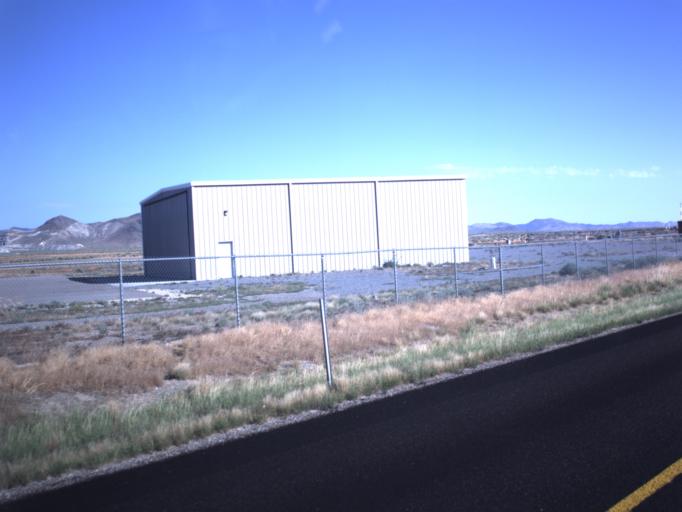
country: US
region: Utah
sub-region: Beaver County
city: Milford
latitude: 38.4198
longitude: -113.0099
